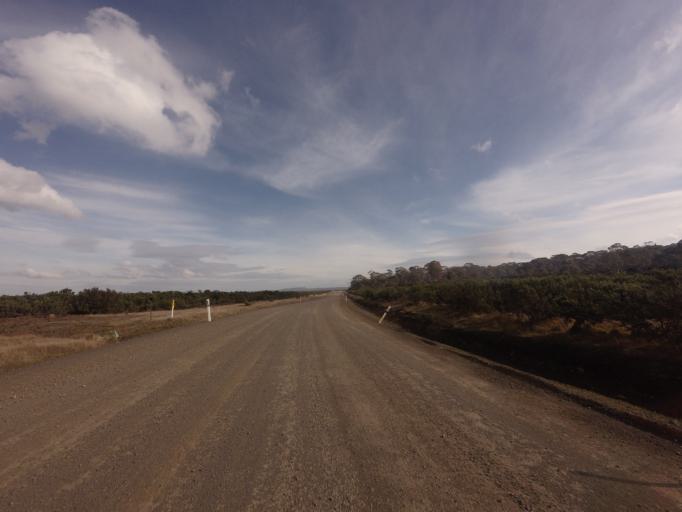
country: AU
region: Tasmania
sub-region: Meander Valley
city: Deloraine
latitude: -41.8940
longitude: 146.6780
